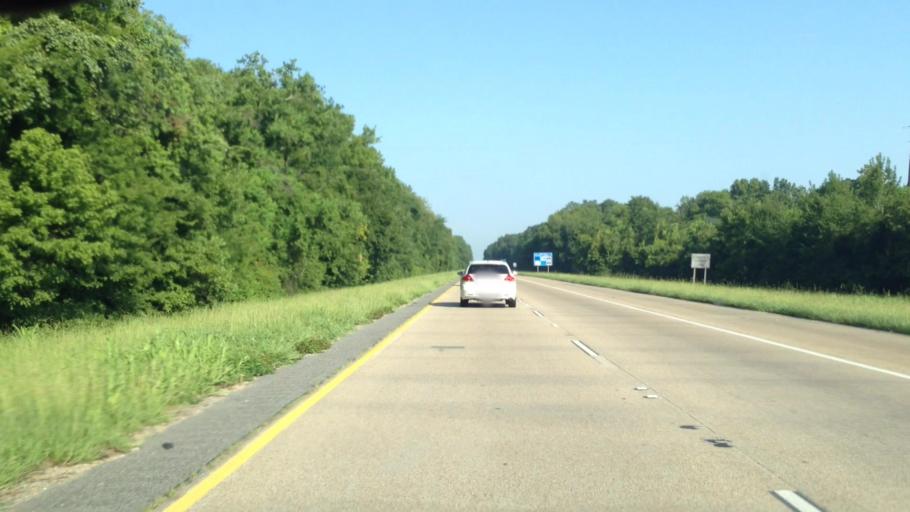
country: US
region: Louisiana
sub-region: Ascension Parish
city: Sorrento
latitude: 30.1843
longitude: -90.9028
